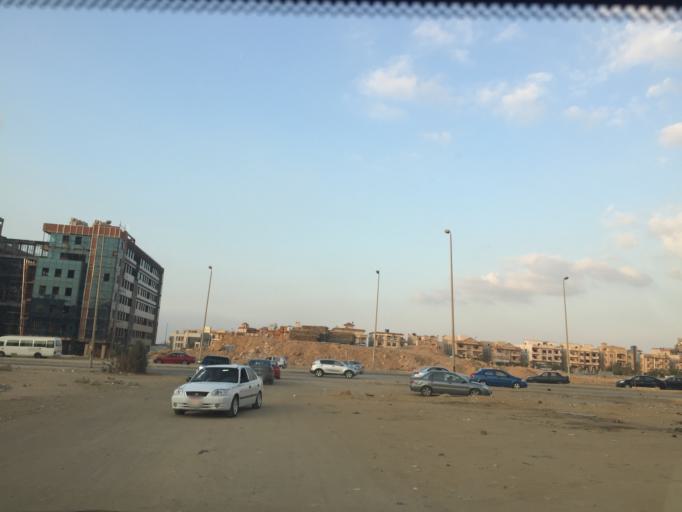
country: EG
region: Muhafazat al Qahirah
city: Cairo
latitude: 30.0193
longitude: 31.4257
